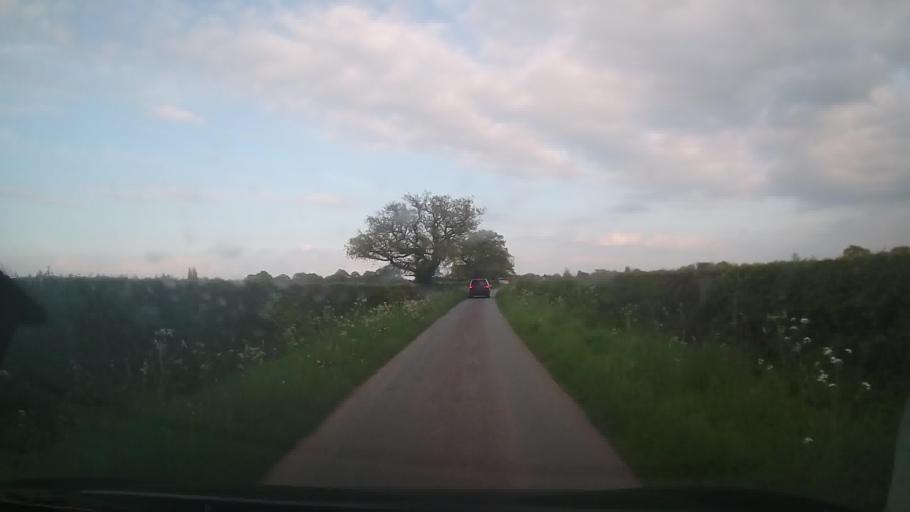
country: GB
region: England
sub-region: Shropshire
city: Ellesmere
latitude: 52.9313
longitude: -2.8410
